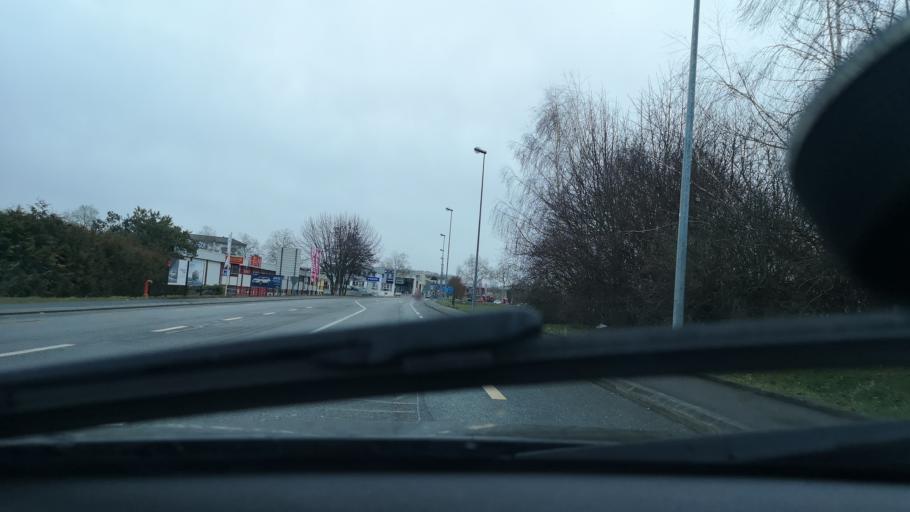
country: CH
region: Vaud
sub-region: Jura-Nord vaudois District
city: Montagny
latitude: 46.7892
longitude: 6.6256
